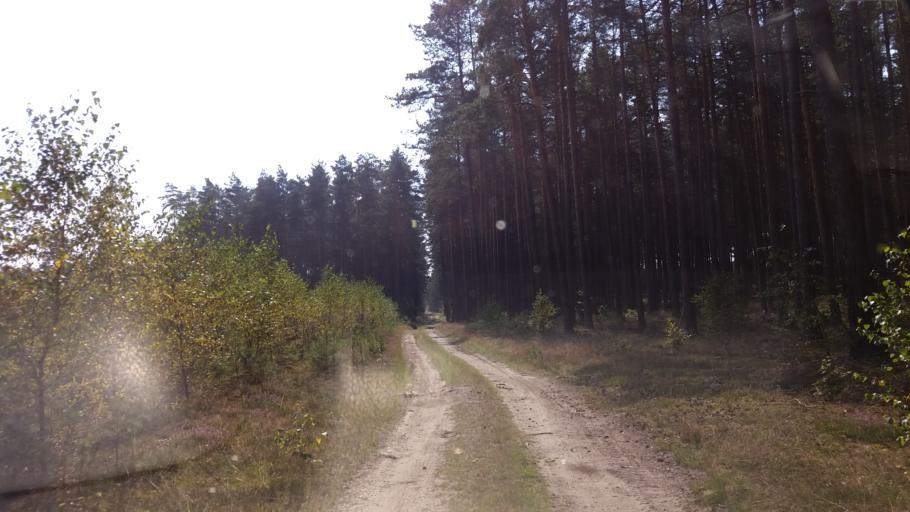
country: PL
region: West Pomeranian Voivodeship
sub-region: Powiat drawski
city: Kalisz Pomorski
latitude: 53.2013
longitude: 15.8942
